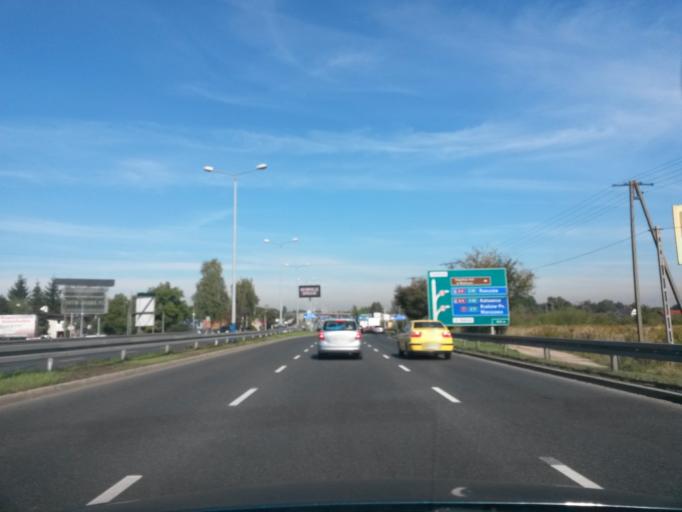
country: PL
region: Lesser Poland Voivodeship
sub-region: Powiat krakowski
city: Libertow
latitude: 49.9856
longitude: 19.9138
